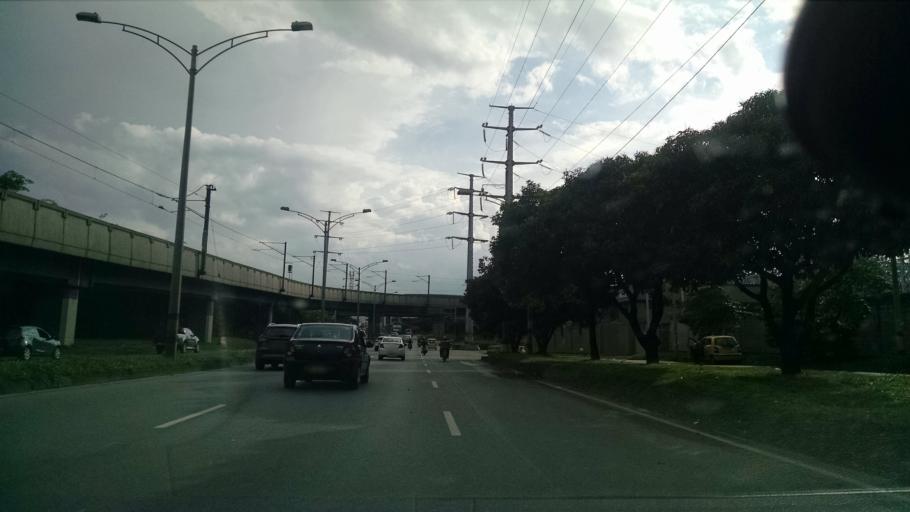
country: CO
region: Antioquia
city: Medellin
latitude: 6.2529
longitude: -75.5786
